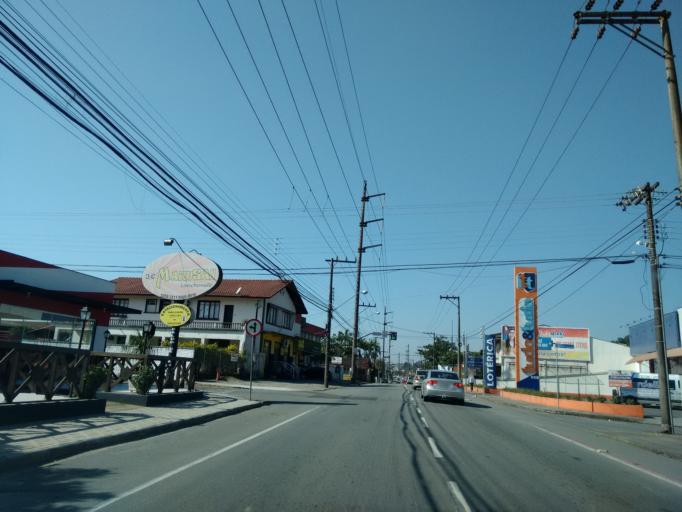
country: BR
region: Santa Catarina
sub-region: Jaragua Do Sul
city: Jaragua do Sul
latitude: -26.4921
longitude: -49.0648
